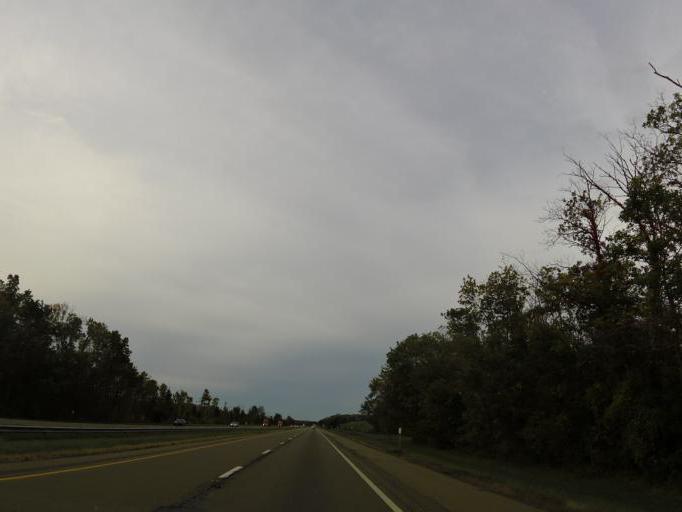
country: US
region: New York
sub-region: Chautauqua County
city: Dunkirk
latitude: 42.4909
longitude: -79.2467
